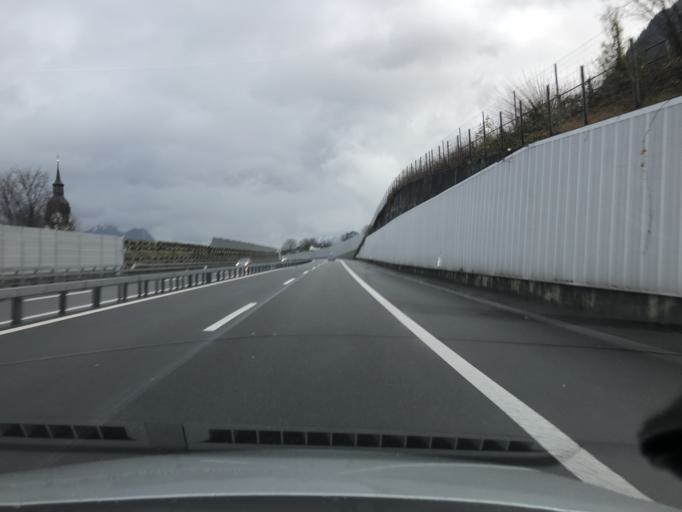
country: CH
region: Nidwalden
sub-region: Nidwalden
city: Buochs
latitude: 46.9705
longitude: 8.4173
